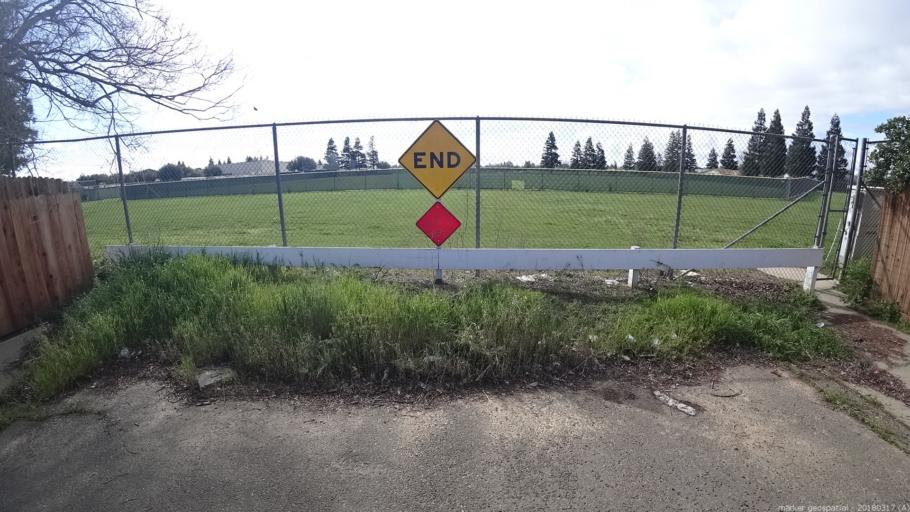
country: US
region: California
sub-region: Sacramento County
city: Florin
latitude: 38.4708
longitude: -121.3946
